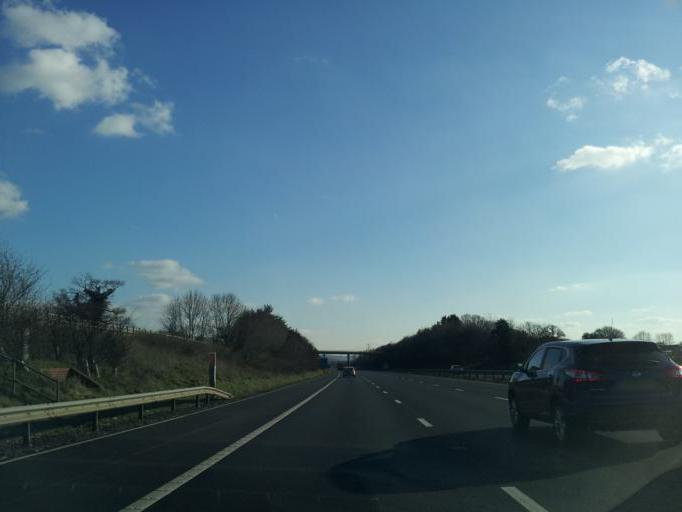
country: GB
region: England
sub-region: Devon
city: Cullompton
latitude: 50.8850
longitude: -3.3793
